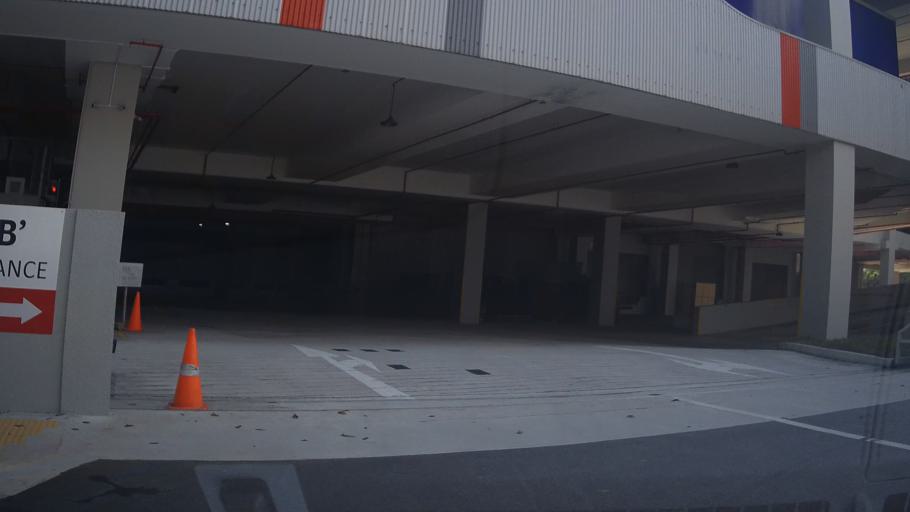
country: SG
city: Singapore
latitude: 1.3320
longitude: 103.9610
